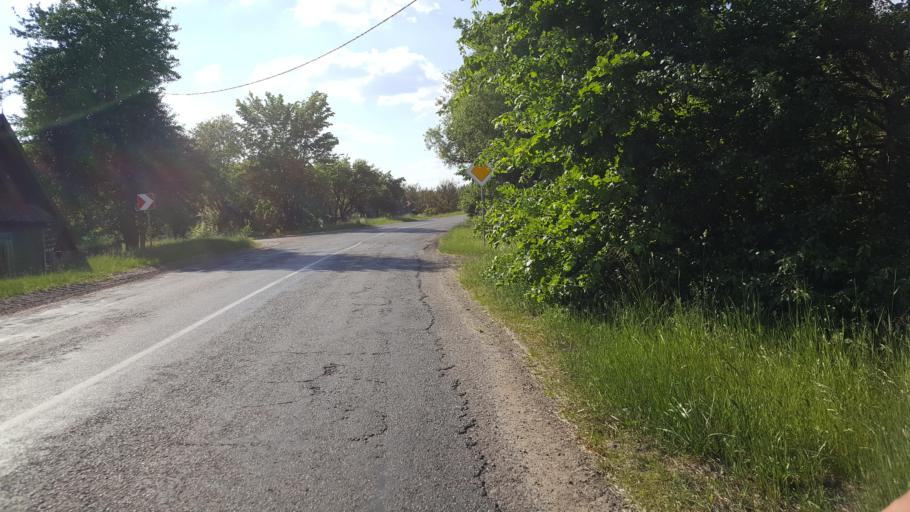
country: BY
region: Brest
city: Zhabinka
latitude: 52.3673
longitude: 24.1424
